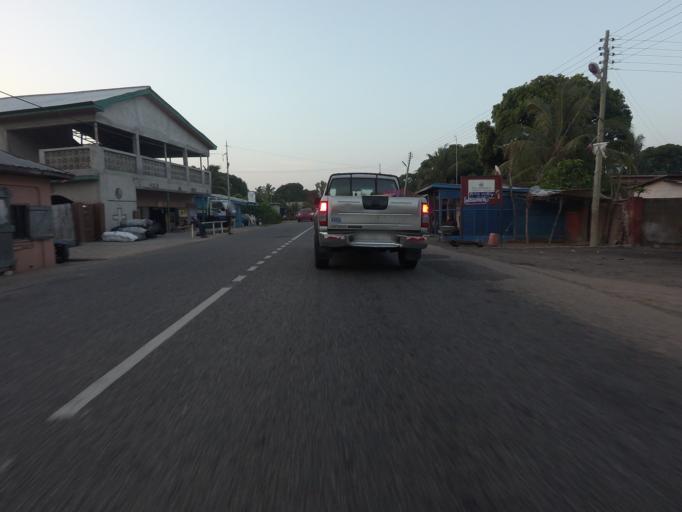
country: GH
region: Volta
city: Keta
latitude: 5.8661
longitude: 0.9787
